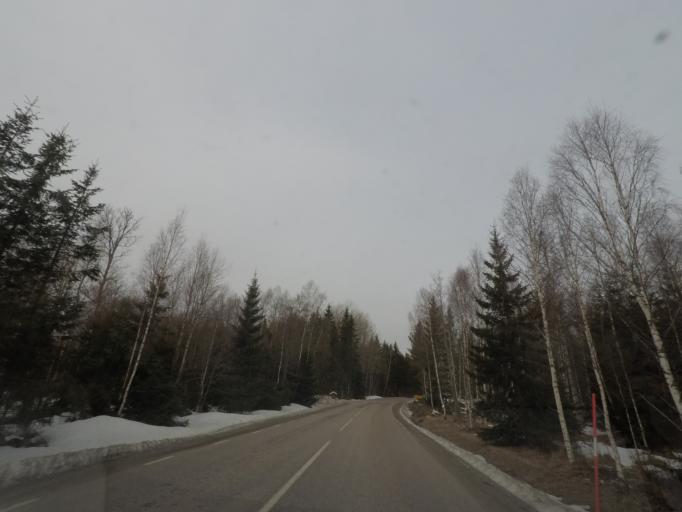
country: SE
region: Vaestmanland
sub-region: Vasteras
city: Skultuna
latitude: 59.7420
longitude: 16.3785
